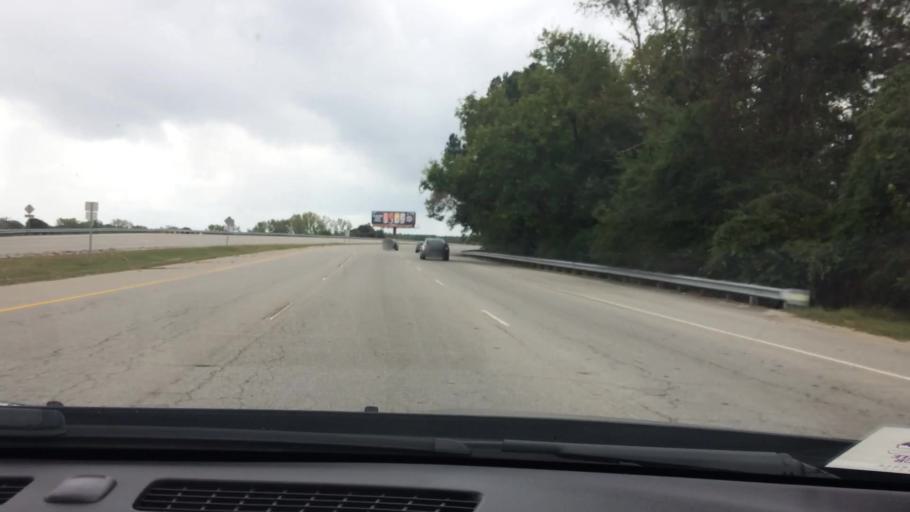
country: US
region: North Carolina
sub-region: Wake County
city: Raleigh
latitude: 35.7617
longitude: -78.6357
